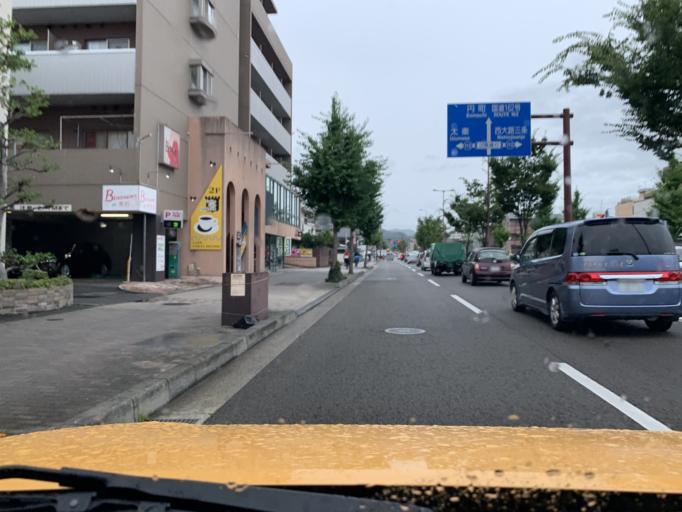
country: JP
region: Kyoto
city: Kyoto
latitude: 35.0066
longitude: 135.7195
